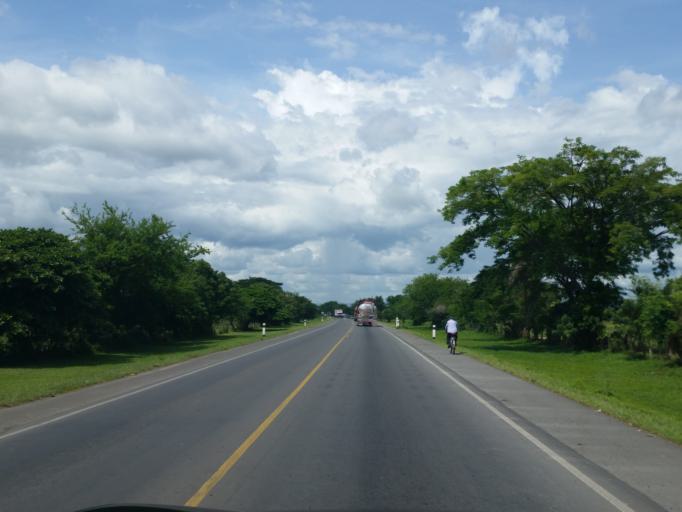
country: NI
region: Managua
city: Tipitapa
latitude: 12.1789
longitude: -86.1114
